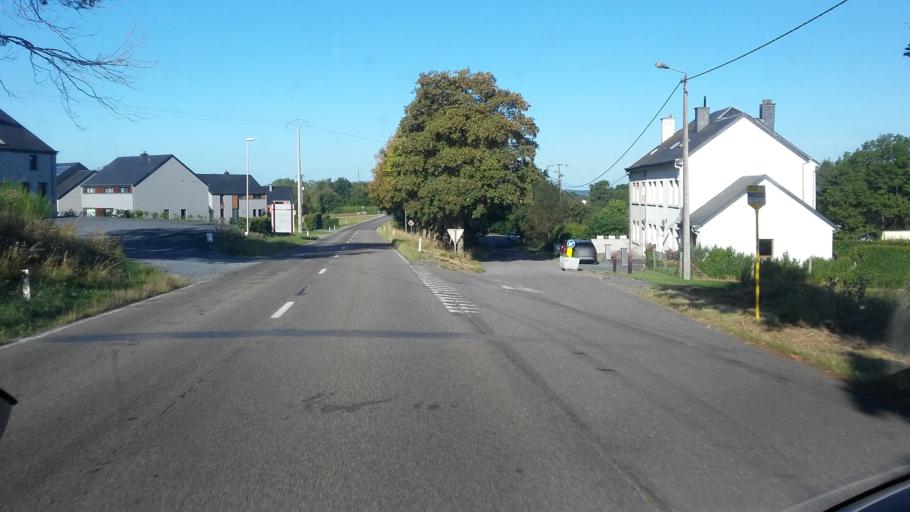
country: BE
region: Wallonia
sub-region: Province du Luxembourg
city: Neufchateau
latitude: 49.8362
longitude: 5.4669
